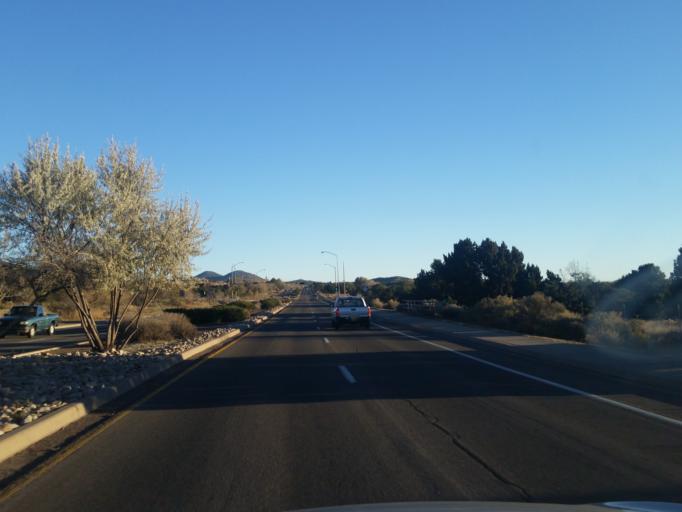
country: US
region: New Mexico
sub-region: Santa Fe County
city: Santa Fe
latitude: 35.6533
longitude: -105.9376
